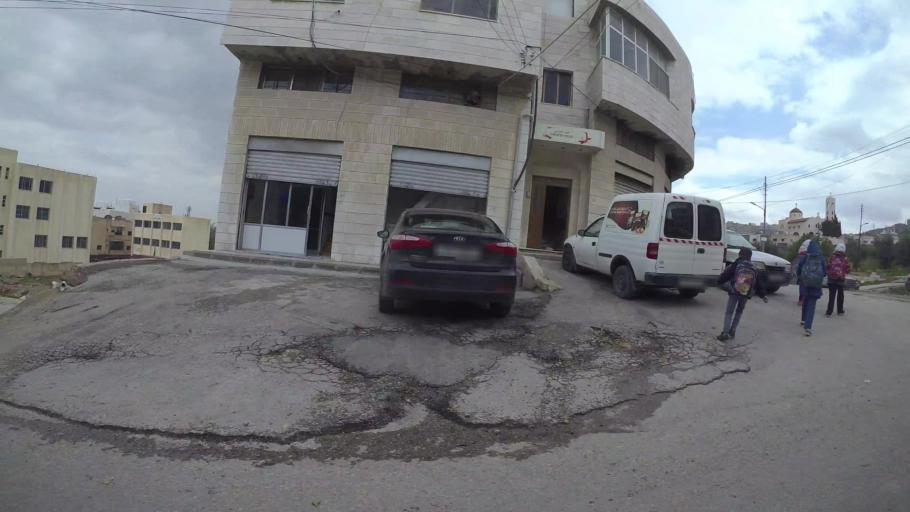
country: JO
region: Amman
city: Al Jubayhah
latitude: 32.0374
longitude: 35.8304
